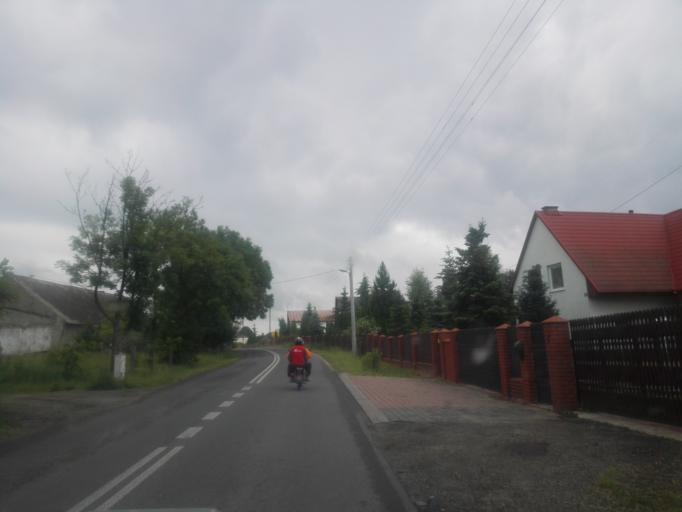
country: PL
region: Silesian Voivodeship
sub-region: Powiat czestochowski
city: Olsztyn
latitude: 50.7418
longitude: 19.3289
